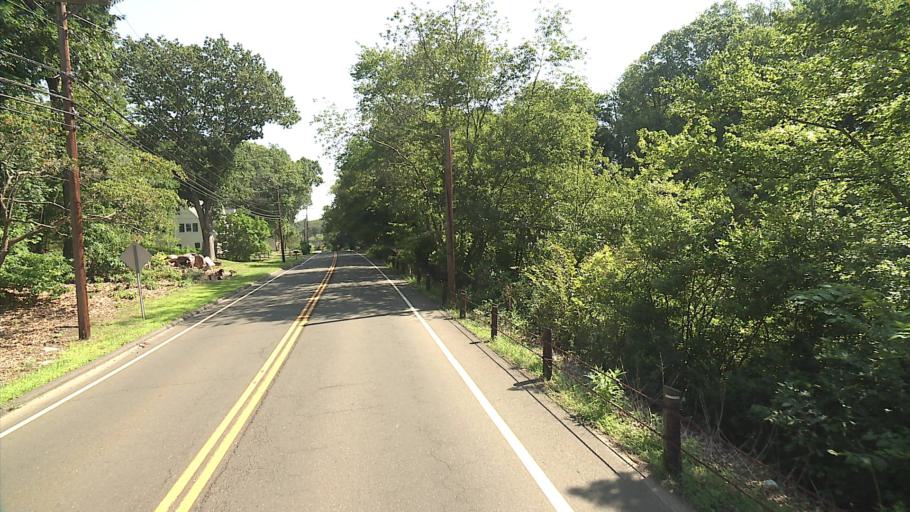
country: US
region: Connecticut
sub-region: New Haven County
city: Guilford Center
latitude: 41.2666
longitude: -72.6978
